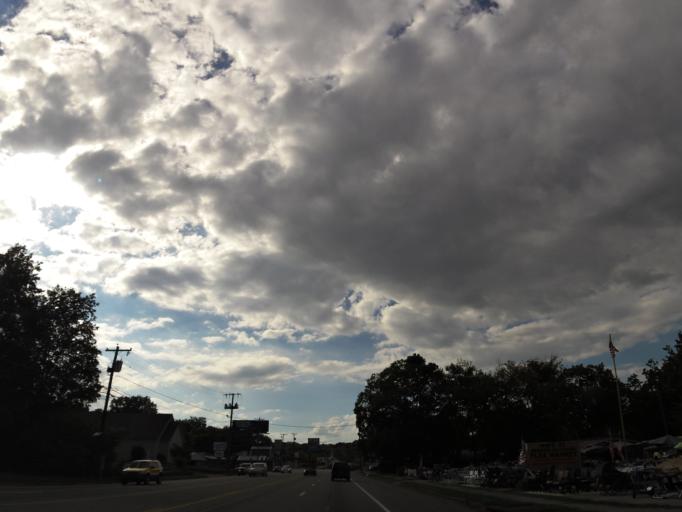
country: US
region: Georgia
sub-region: Catoosa County
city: Lakeview
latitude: 34.9694
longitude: -85.2661
